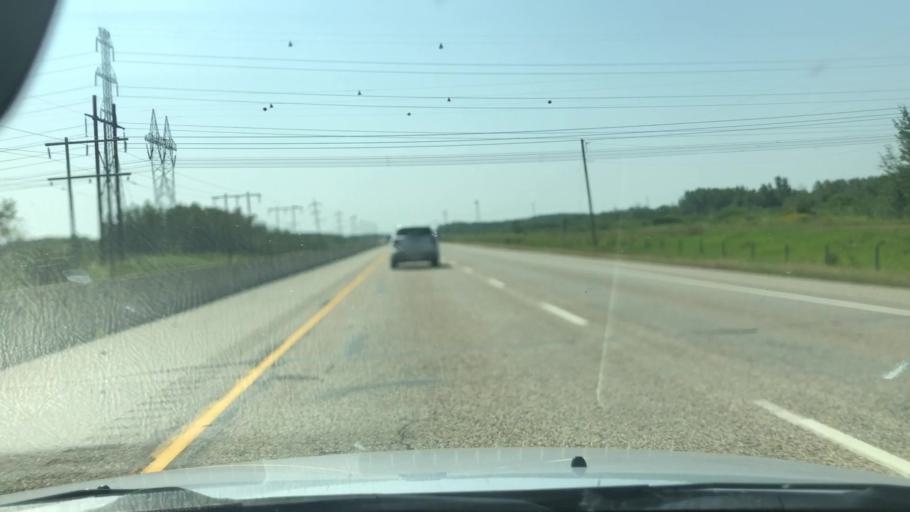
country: CA
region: Alberta
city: Devon
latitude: 53.4627
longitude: -113.7626
